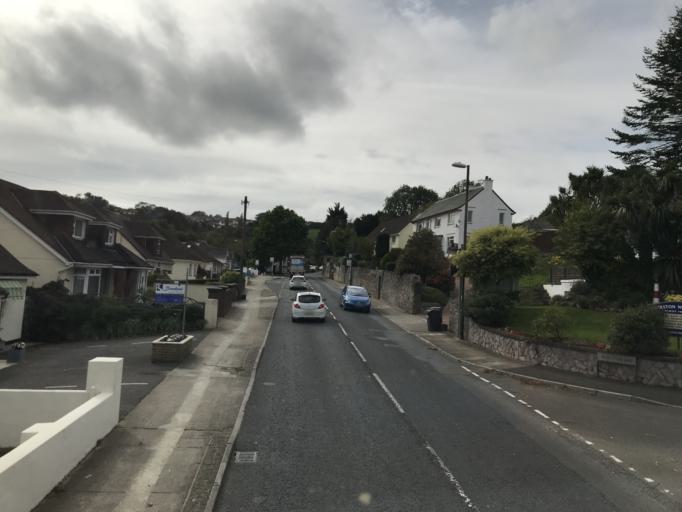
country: GB
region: England
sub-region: Borough of Torbay
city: Brixham
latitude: 50.3902
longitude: -3.5263
